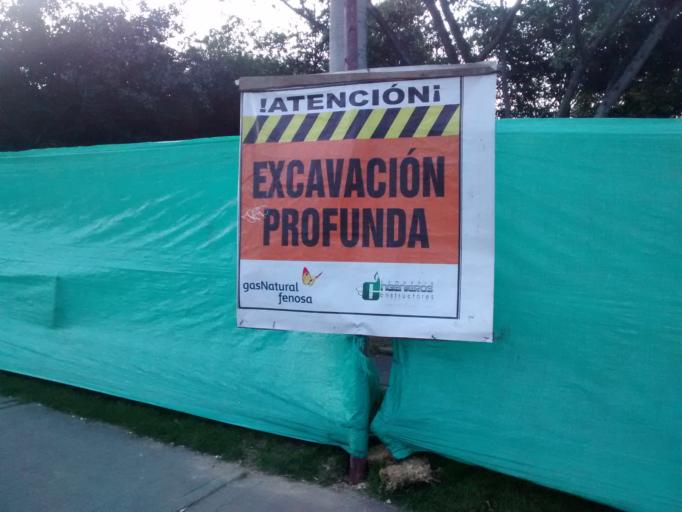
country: CO
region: Bogota D.C.
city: Bogota
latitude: 4.6667
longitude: -74.1300
